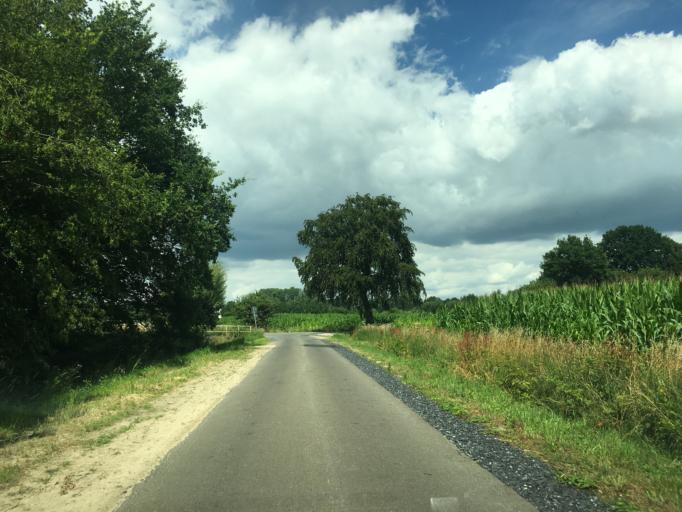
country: DE
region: North Rhine-Westphalia
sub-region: Regierungsbezirk Munster
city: Greven
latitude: 52.0304
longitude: 7.6097
